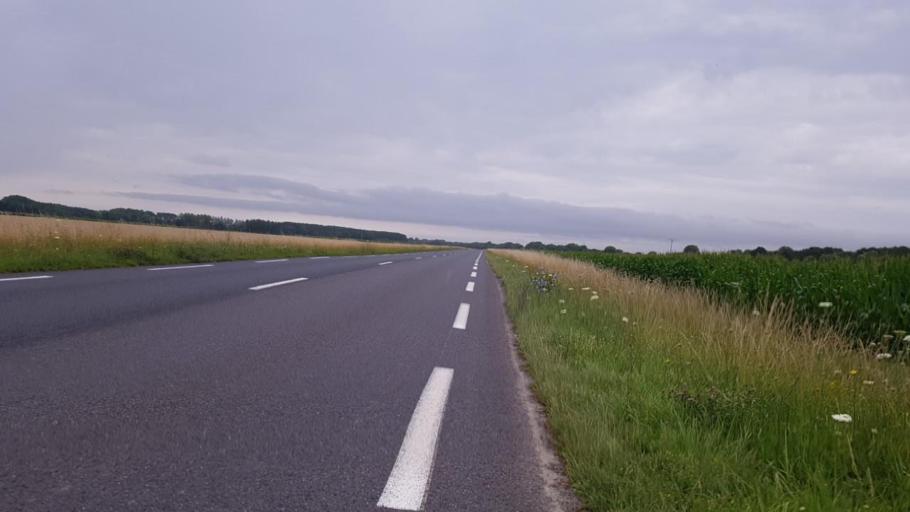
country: FR
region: Champagne-Ardenne
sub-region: Departement de la Marne
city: Pargny-sur-Saulx
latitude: 48.7567
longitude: 4.7345
